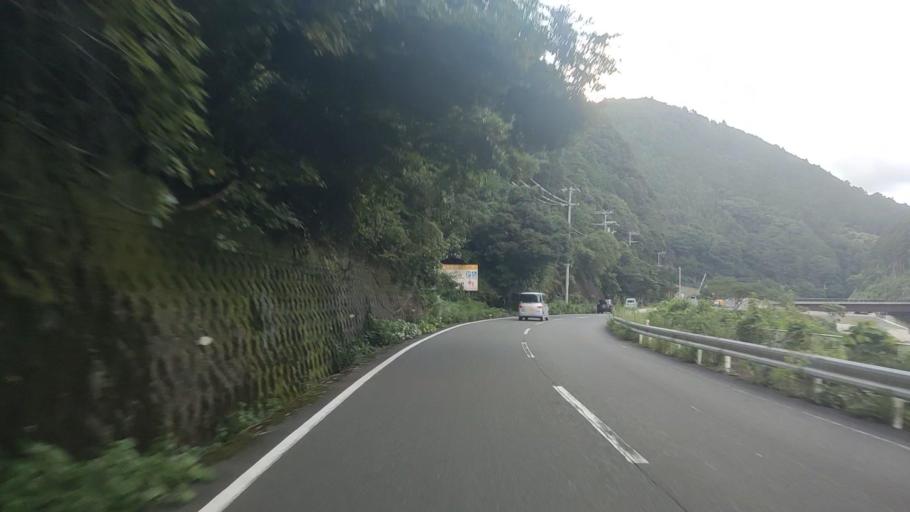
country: JP
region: Wakayama
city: Tanabe
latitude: 33.7700
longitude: 135.4998
